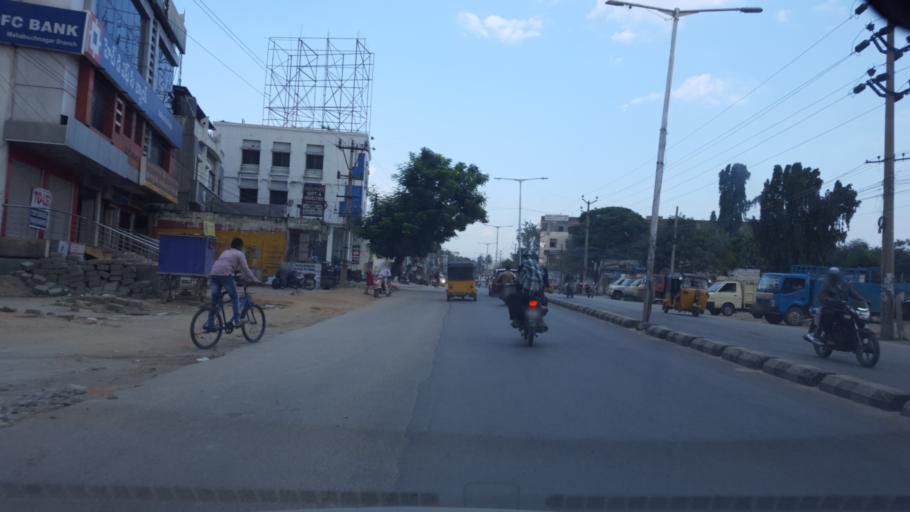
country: IN
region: Telangana
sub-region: Mahbubnagar
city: Mahbubnagar
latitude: 16.7501
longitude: 78.0054
